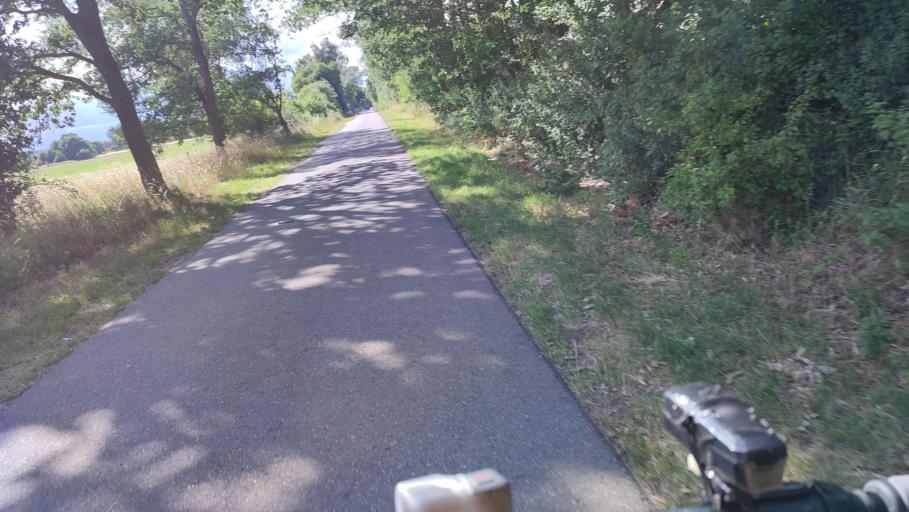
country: DE
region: Lower Saxony
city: Neu Darchau
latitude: 53.2384
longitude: 10.9080
